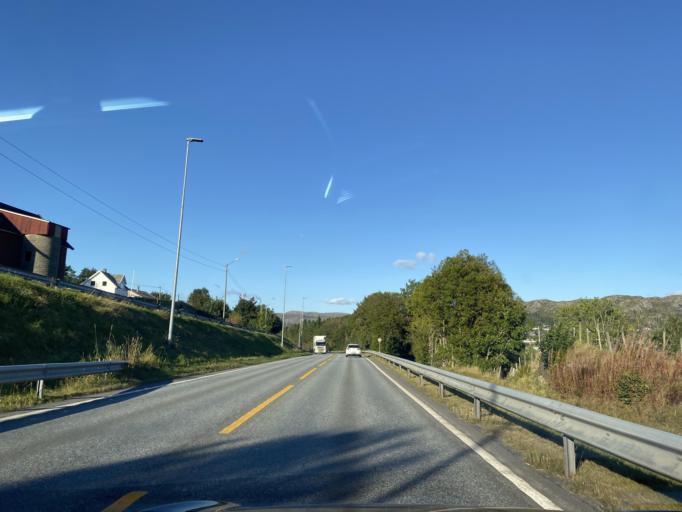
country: NO
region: Rogaland
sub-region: Karmoy
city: Eike
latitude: 59.4183
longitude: 5.3745
